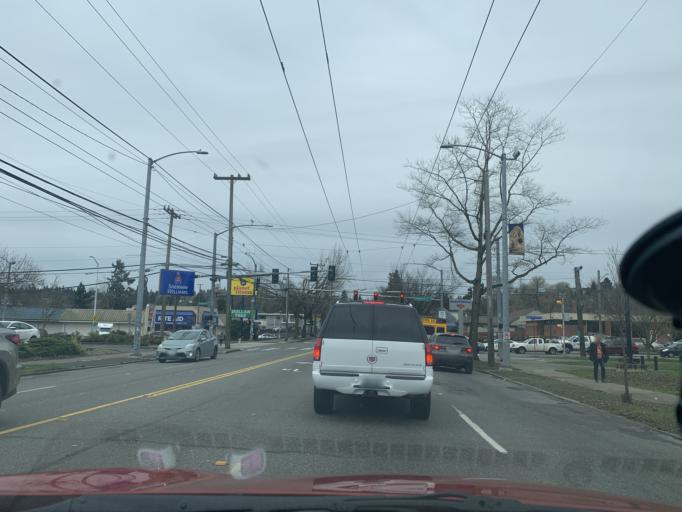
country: US
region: Washington
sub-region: King County
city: Bryn Mawr-Skyway
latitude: 47.5238
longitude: -122.2700
